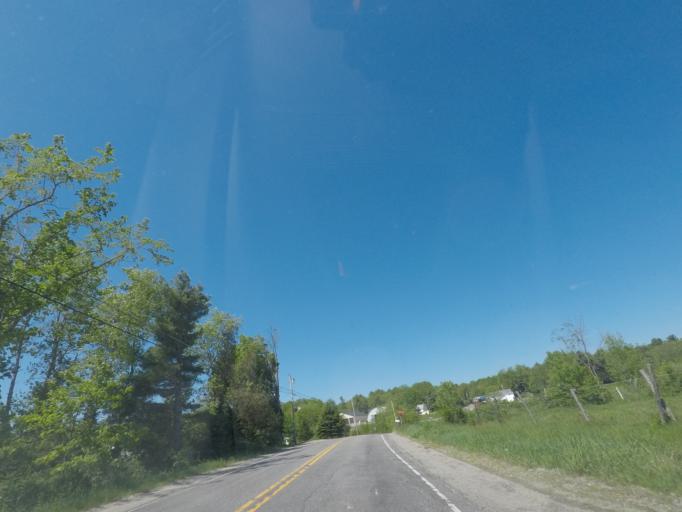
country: US
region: Maine
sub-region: Kennebec County
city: Manchester
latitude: 44.2278
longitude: -69.8744
